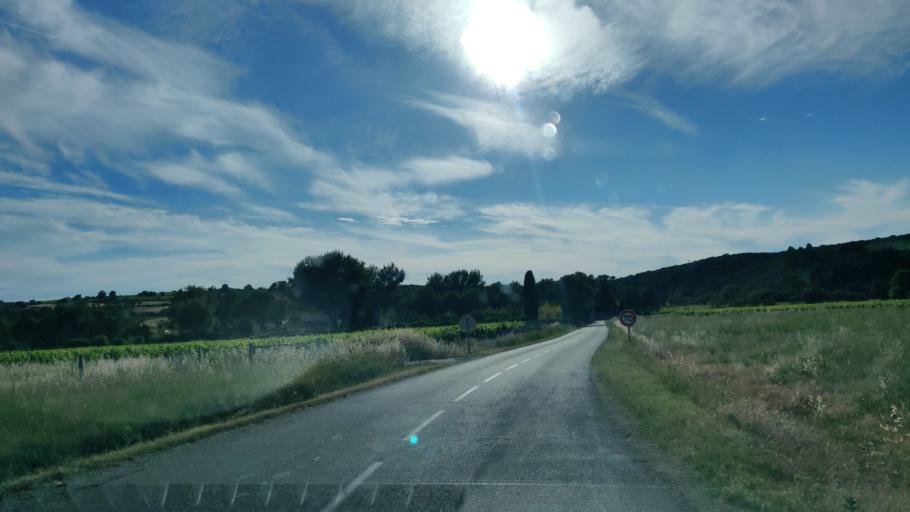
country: FR
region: Languedoc-Roussillon
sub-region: Departement de l'Herault
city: Combaillaux
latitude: 43.6626
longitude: 3.7702
